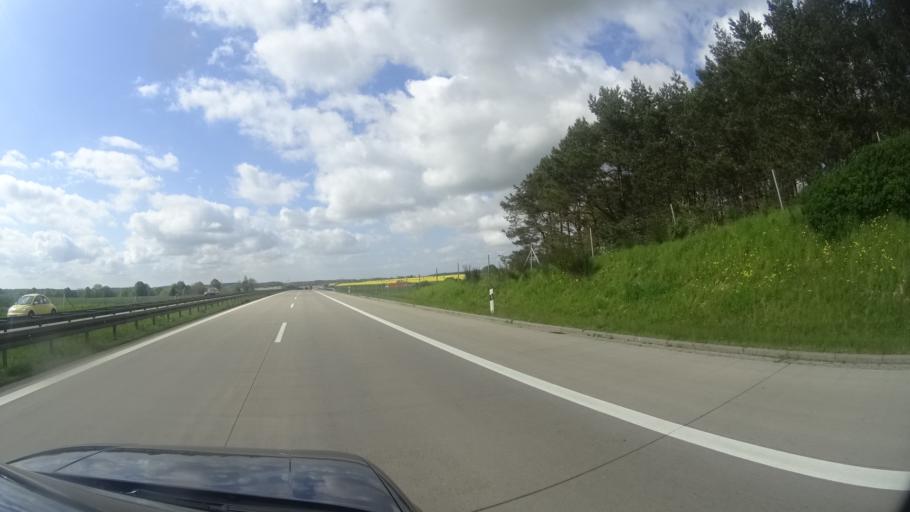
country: DE
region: Mecklenburg-Vorpommern
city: Kavelstorf
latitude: 53.9373
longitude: 12.2151
